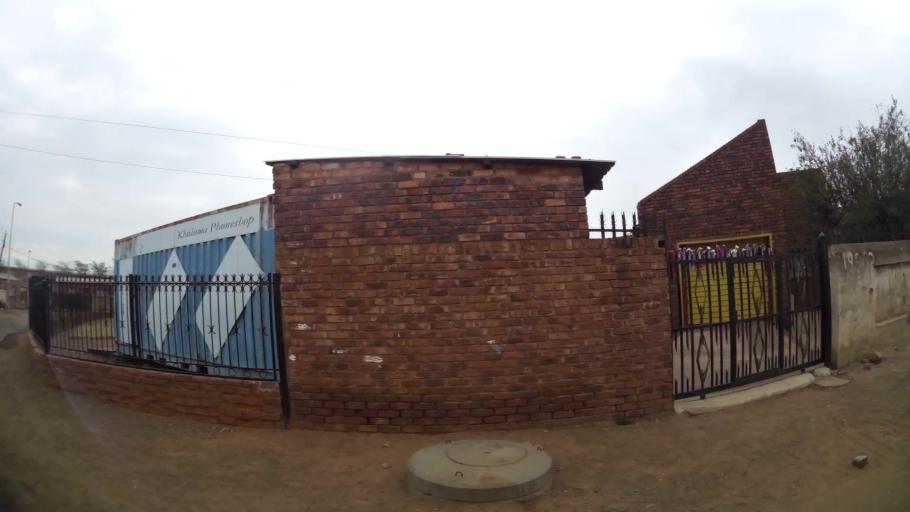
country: ZA
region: Gauteng
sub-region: City of Tshwane Metropolitan Municipality
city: Pretoria
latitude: -25.7125
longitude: 28.3356
